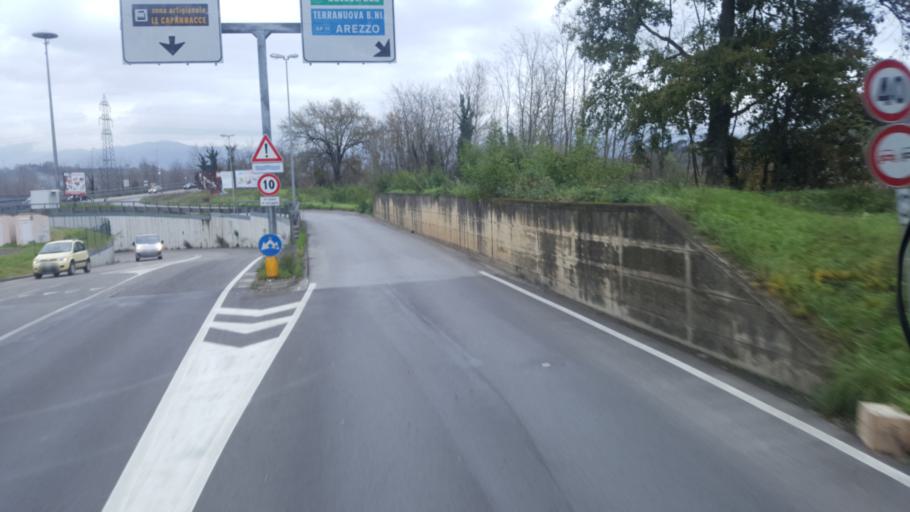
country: IT
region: Tuscany
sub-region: Province of Arezzo
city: Montevarchi
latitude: 43.5385
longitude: 11.5638
